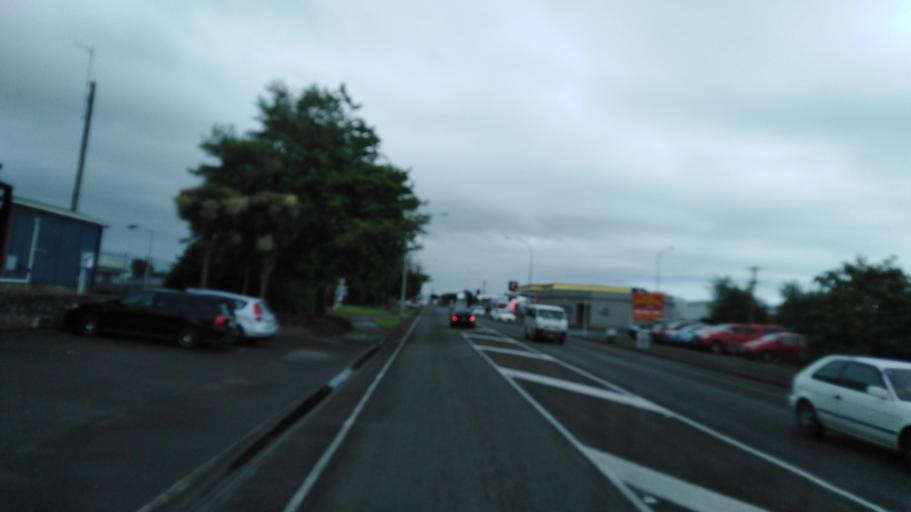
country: NZ
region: Manawatu-Wanganui
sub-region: Horowhenua District
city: Levin
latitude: -40.6313
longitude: 175.2774
